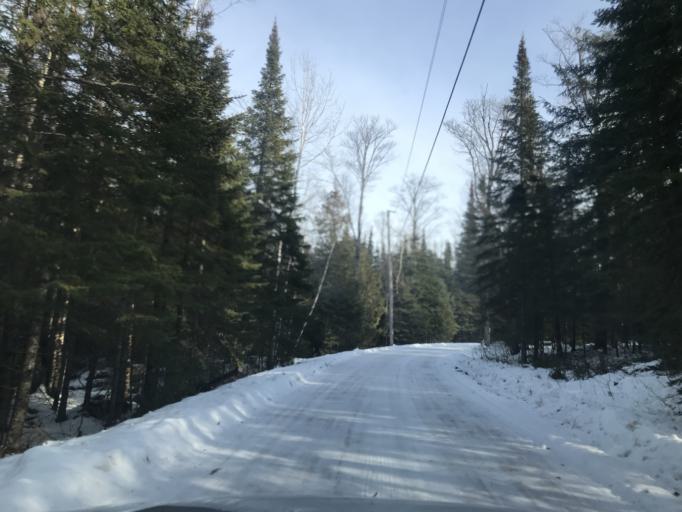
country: US
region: Wisconsin
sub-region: Door County
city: Sturgeon Bay
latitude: 45.1550
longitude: -87.0481
